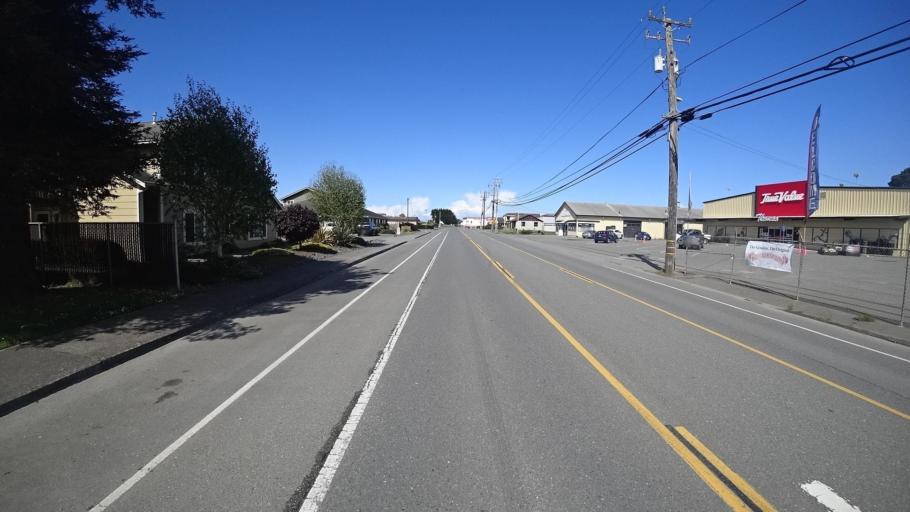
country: US
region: California
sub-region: Humboldt County
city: McKinleyville
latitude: 40.9360
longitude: -124.0982
